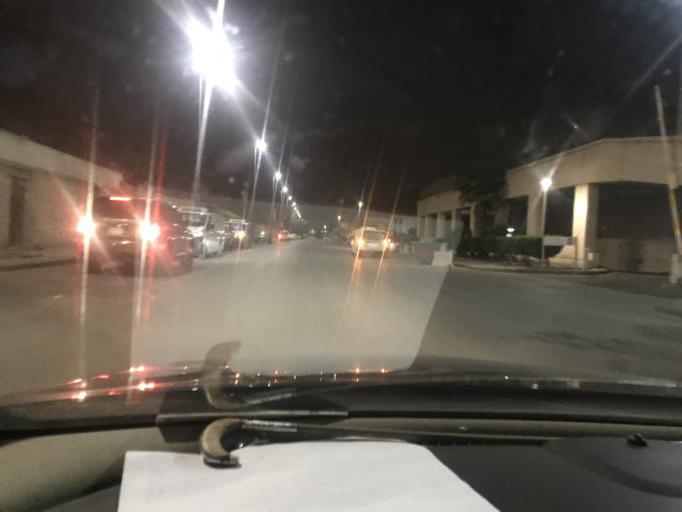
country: SA
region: Ar Riyad
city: Riyadh
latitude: 24.7232
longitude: 46.7743
